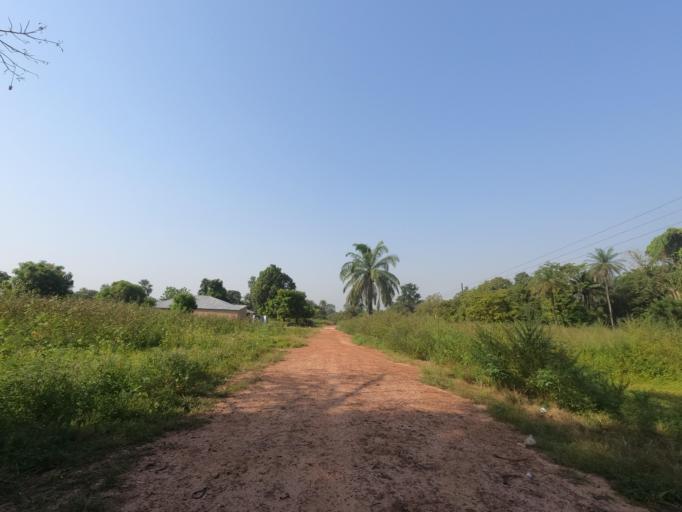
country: SN
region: Sedhiou
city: Sedhiou
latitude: 12.4455
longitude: -15.7392
